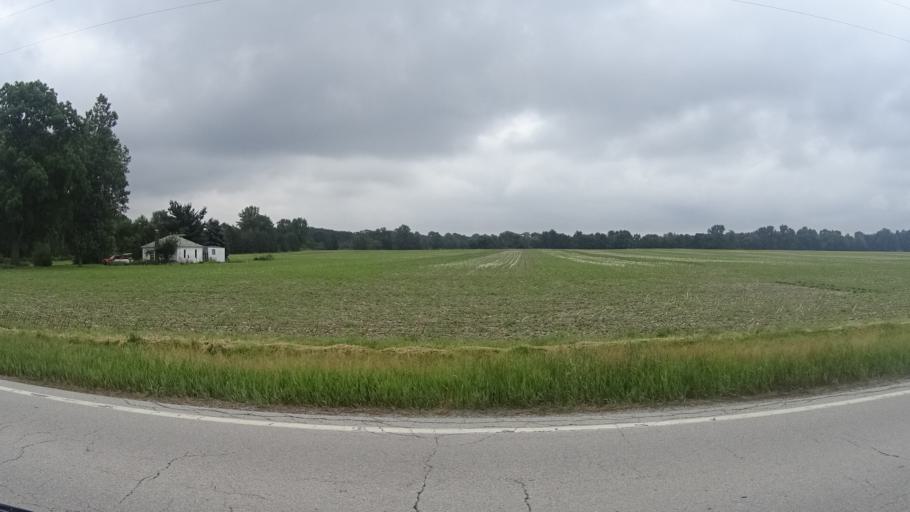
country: US
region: Ohio
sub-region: Erie County
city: Milan
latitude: 41.2994
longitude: -82.5627
